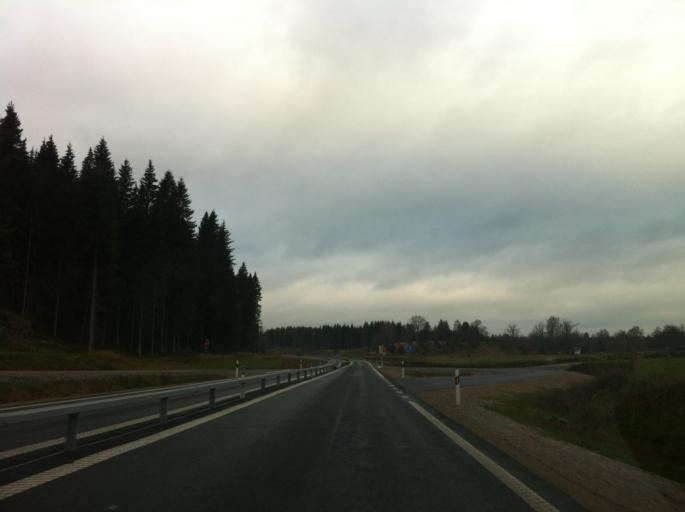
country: SE
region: Joenkoeping
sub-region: Vetlanda Kommun
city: Vetlanda
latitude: 57.4148
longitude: 15.2510
